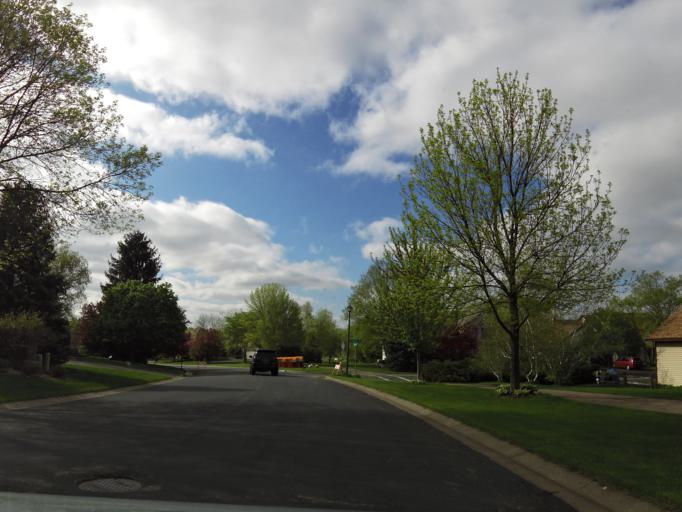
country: US
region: Minnesota
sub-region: Washington County
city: Woodbury
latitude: 44.9235
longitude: -92.9180
